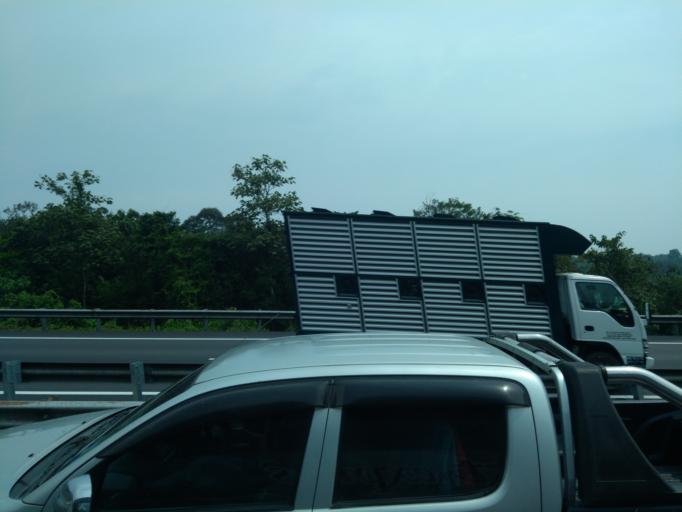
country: MY
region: Perak
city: Kuala Kangsar
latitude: 4.6963
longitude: 100.9649
